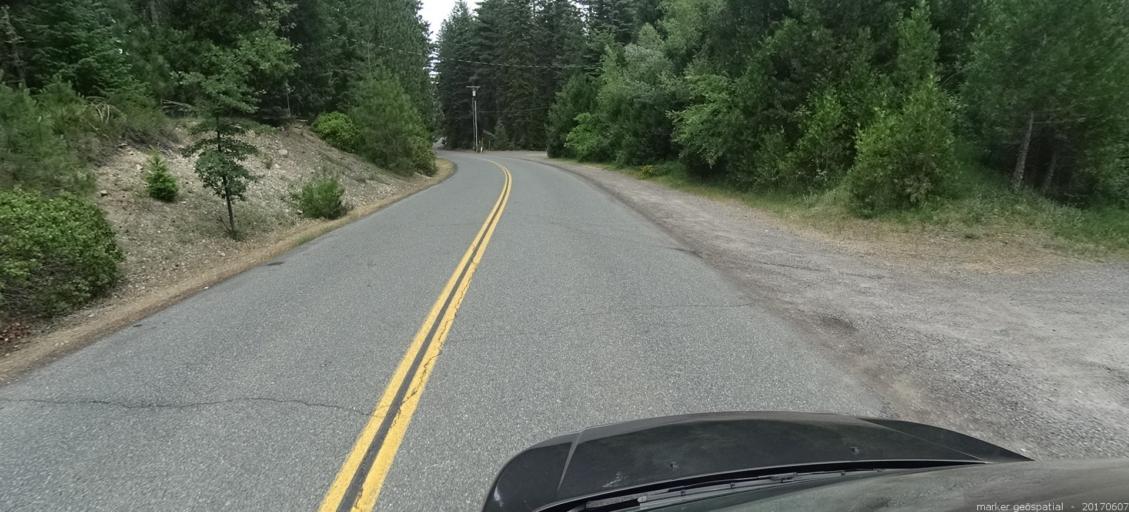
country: US
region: California
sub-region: Siskiyou County
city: Mount Shasta
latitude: 41.3246
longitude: -122.3435
